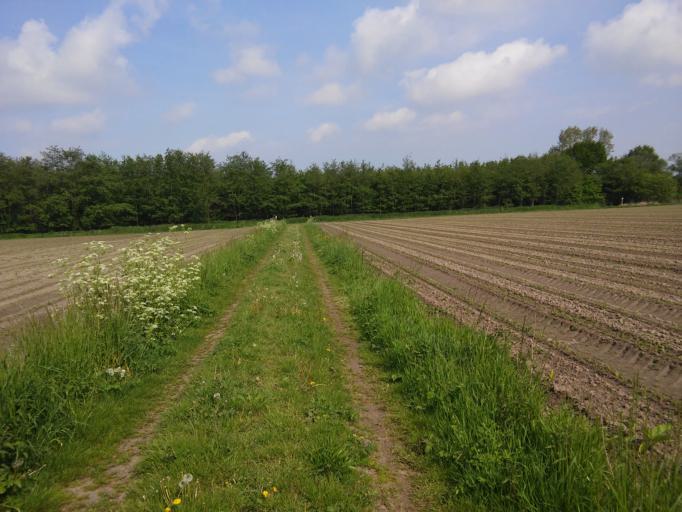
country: BE
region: Flanders
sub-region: Provincie Antwerpen
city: Mechelen
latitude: 51.0254
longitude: 4.4344
